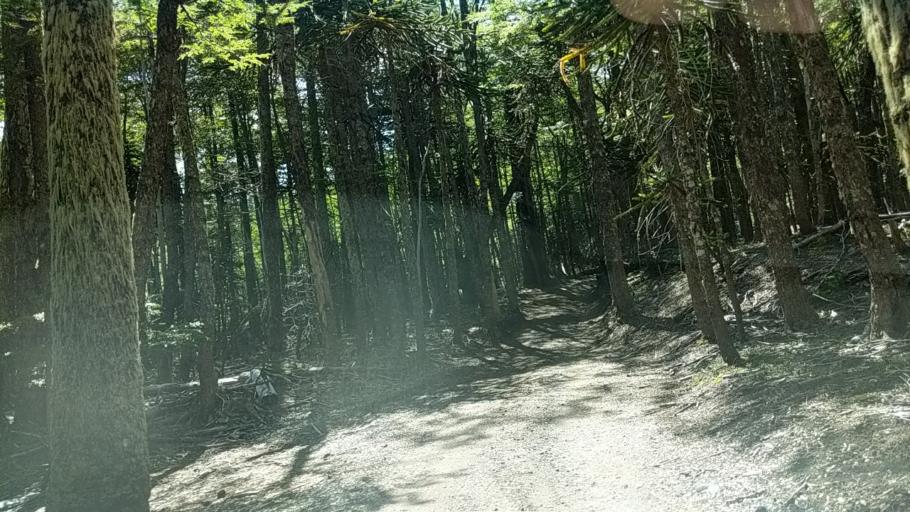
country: CL
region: Araucania
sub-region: Provincia de Cautin
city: Pucon
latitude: -39.4620
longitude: -71.8516
